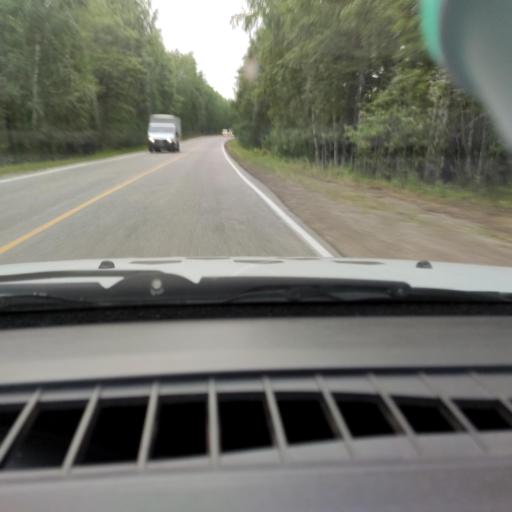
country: RU
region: Chelyabinsk
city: Ozersk
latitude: 55.8368
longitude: 60.6490
